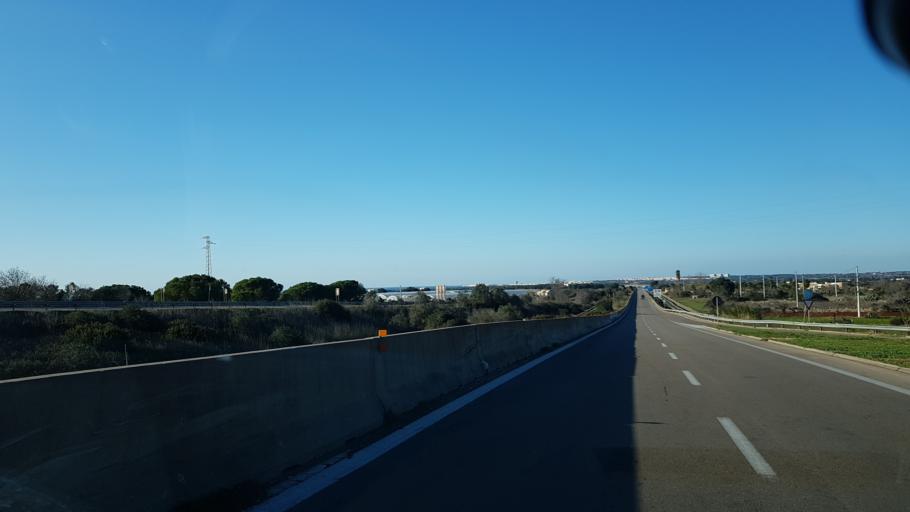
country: IT
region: Apulia
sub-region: Provincia di Lecce
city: Taviano
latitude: 40.0022
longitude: 18.0620
